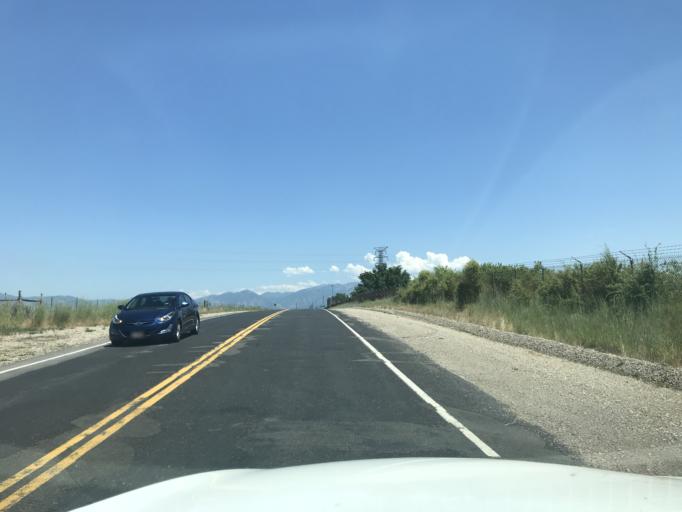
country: US
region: Utah
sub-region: Salt Lake County
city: Magna
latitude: 40.6820
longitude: -112.0862
